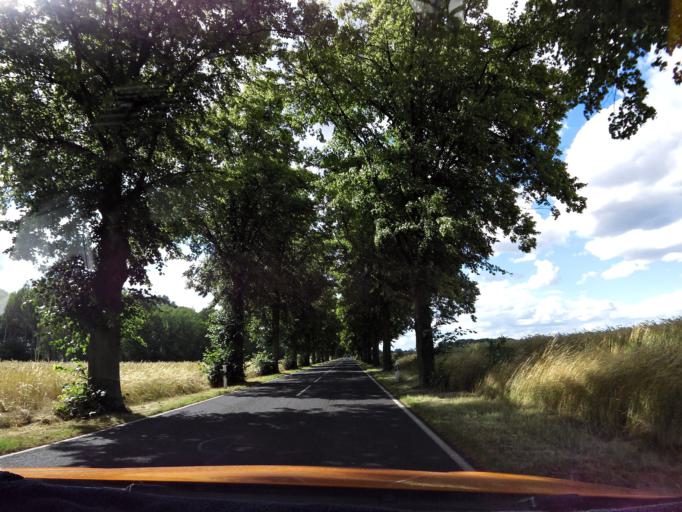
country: DE
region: Brandenburg
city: Mittenwalde
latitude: 52.2982
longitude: 13.5285
